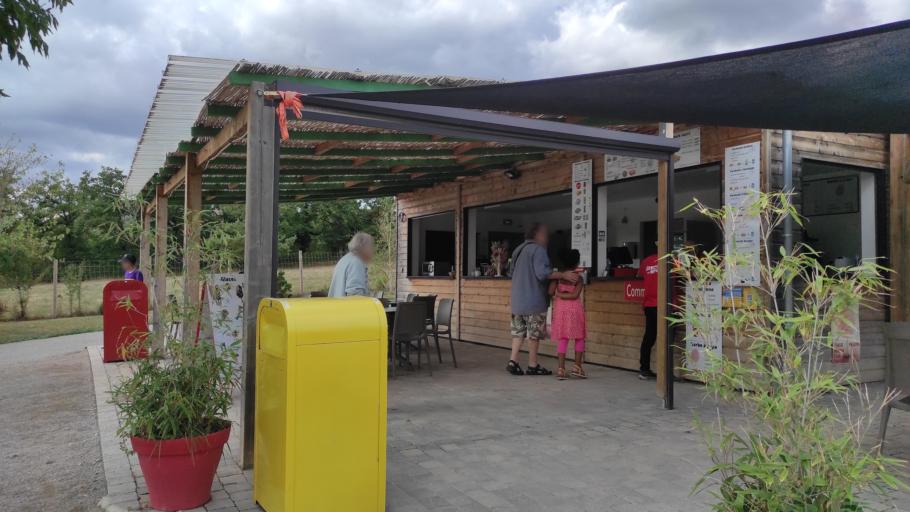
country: FR
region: Midi-Pyrenees
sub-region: Departement de l'Aveyron
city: La Loubiere
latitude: 44.3949
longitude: 2.6929
